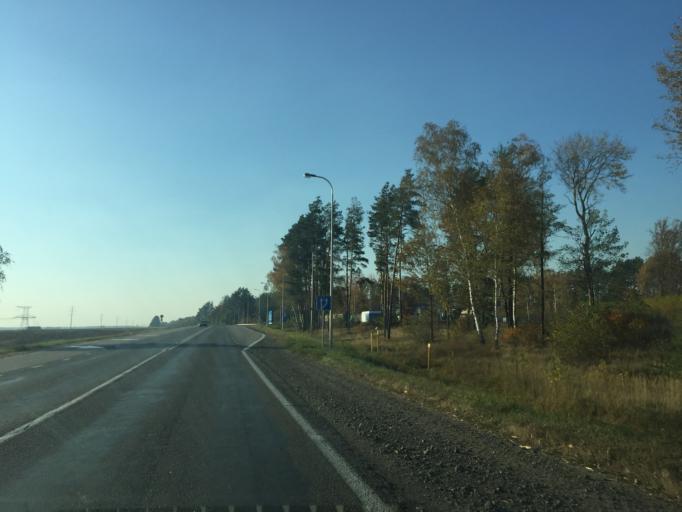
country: BY
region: Gomel
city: Dobrush
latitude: 52.3852
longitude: 31.2797
